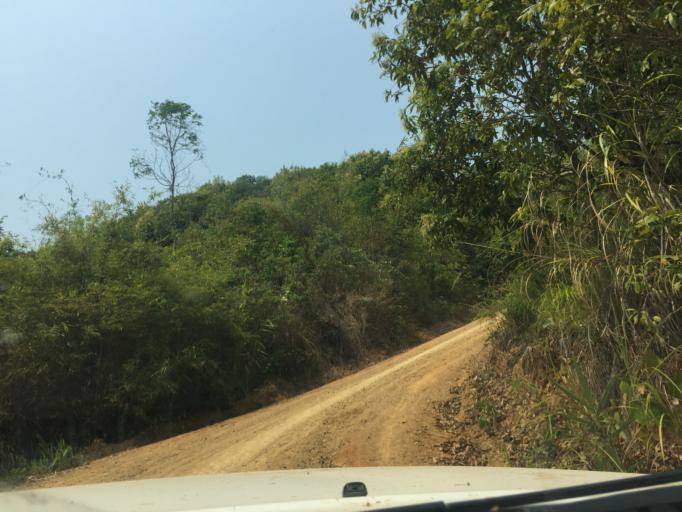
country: LA
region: Loungnamtha
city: Muang Nale
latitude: 20.6300
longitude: 101.6402
